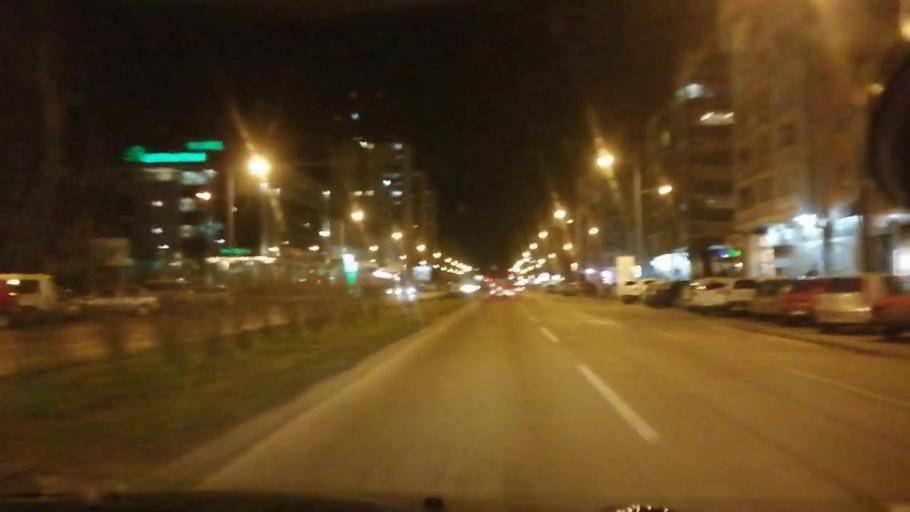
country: RS
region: Autonomna Pokrajina Vojvodina
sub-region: Juznobacki Okrug
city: Novi Sad
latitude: 45.2412
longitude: 19.8299
